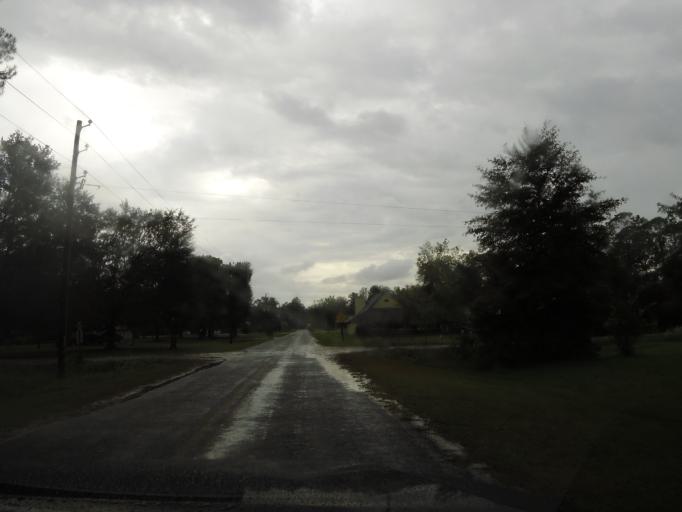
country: US
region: Florida
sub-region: Nassau County
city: Hilliard
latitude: 30.5260
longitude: -82.0369
